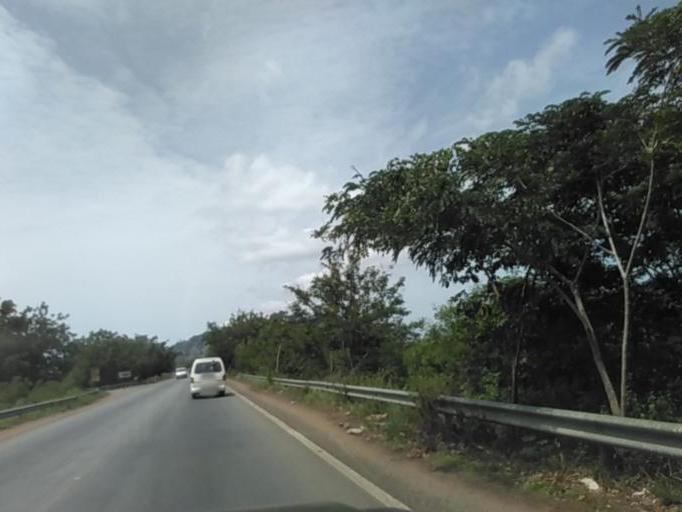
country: GH
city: Akropong
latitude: 6.1175
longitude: 0.0490
